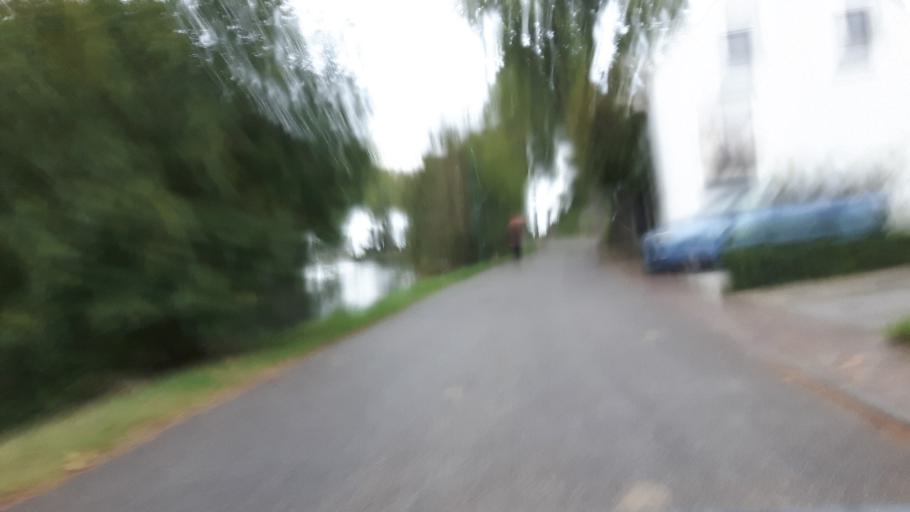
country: NL
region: Utrecht
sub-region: Stichtse Vecht
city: Maarssen
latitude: 52.1296
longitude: 5.0692
